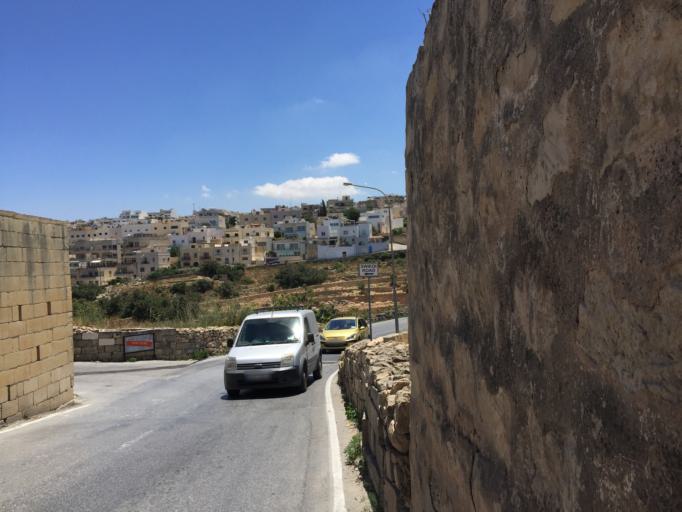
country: MT
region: Is-Swieqi
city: Swieqi
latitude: 35.9182
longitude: 14.4804
